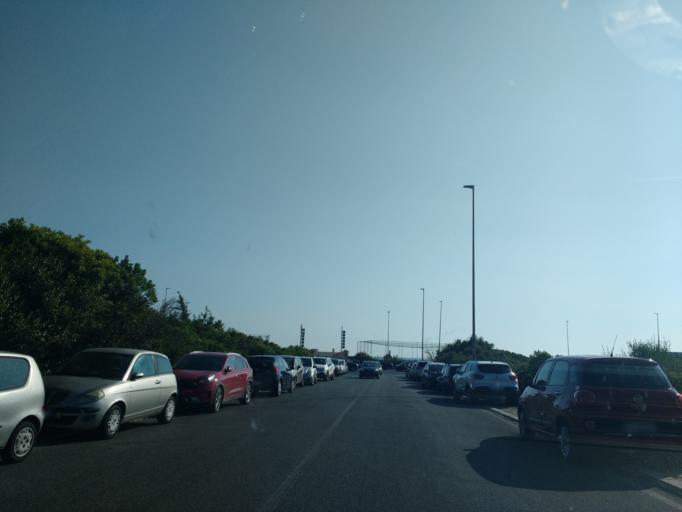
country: IT
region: Latium
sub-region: Citta metropolitana di Roma Capitale
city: Acilia-Castel Fusano-Ostia Antica
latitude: 41.7024
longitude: 12.3465
